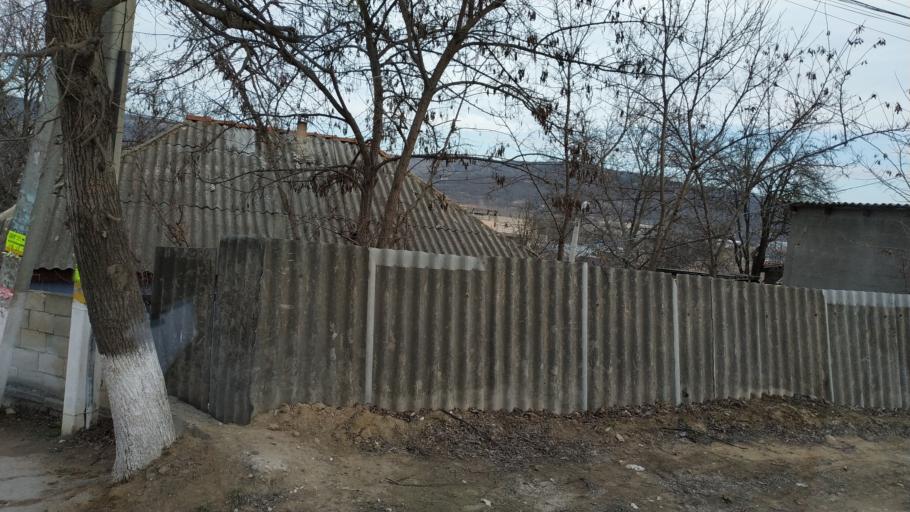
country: MD
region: Nisporeni
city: Nisporeni
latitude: 47.0830
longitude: 28.1752
